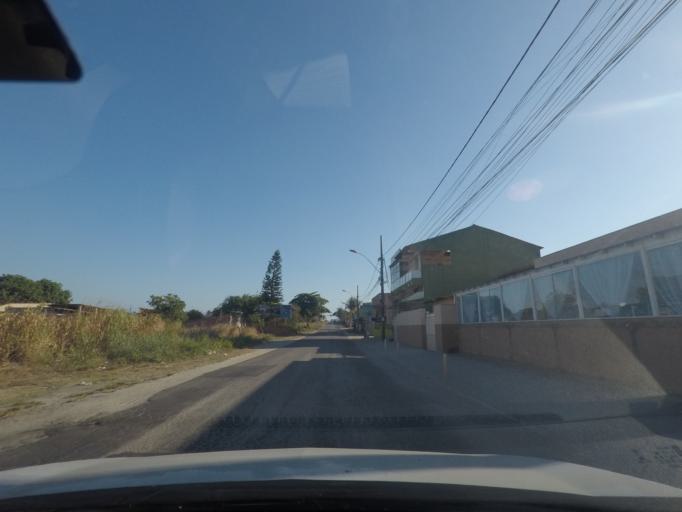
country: BR
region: Rio de Janeiro
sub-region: Marica
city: Marica
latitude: -22.9646
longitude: -42.9424
